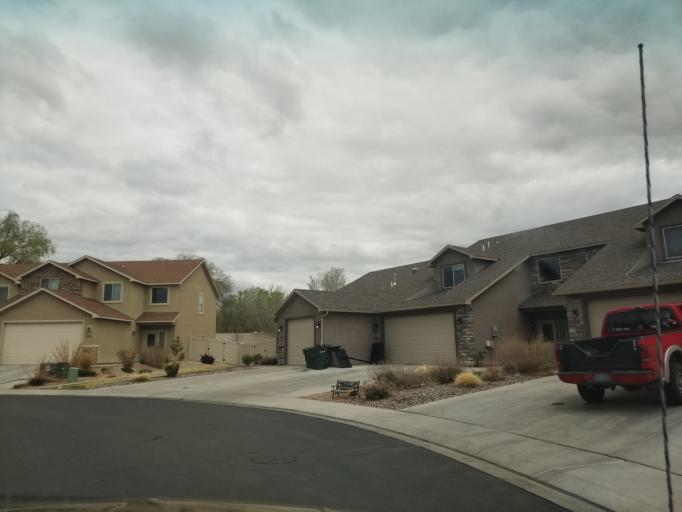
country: US
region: Colorado
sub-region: Mesa County
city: Redlands
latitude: 39.0996
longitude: -108.5912
